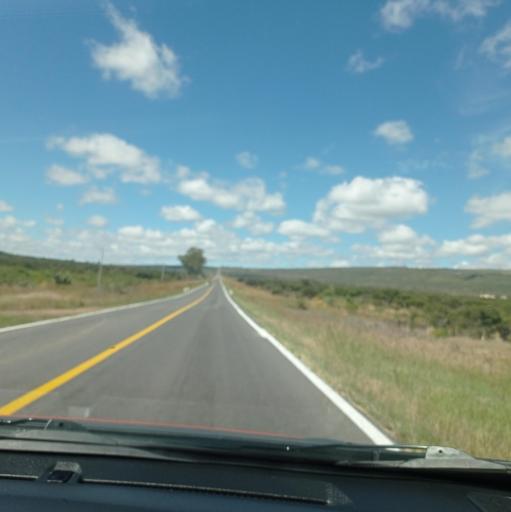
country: MX
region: Jalisco
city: San Miguel el Alto
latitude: 21.0161
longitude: -102.4768
